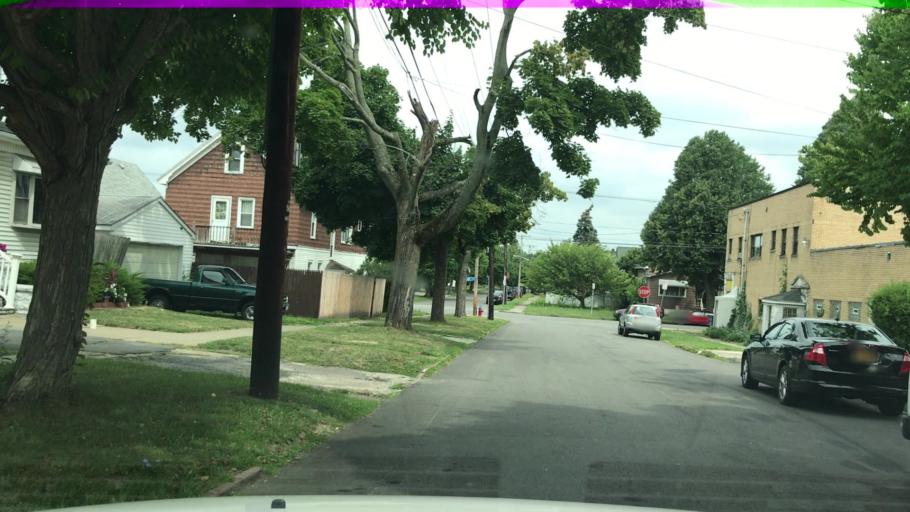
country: US
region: New York
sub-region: Erie County
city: Sloan
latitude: 42.9092
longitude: -78.8015
